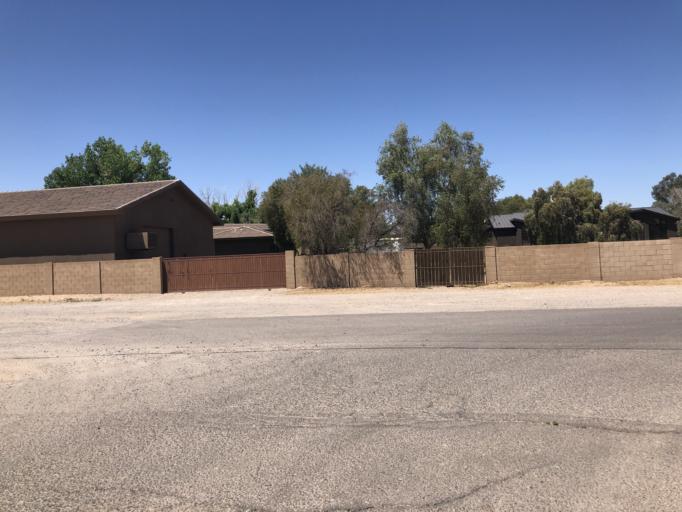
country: US
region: Arizona
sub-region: Maricopa County
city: Sun Lakes
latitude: 33.2293
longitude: -111.8194
